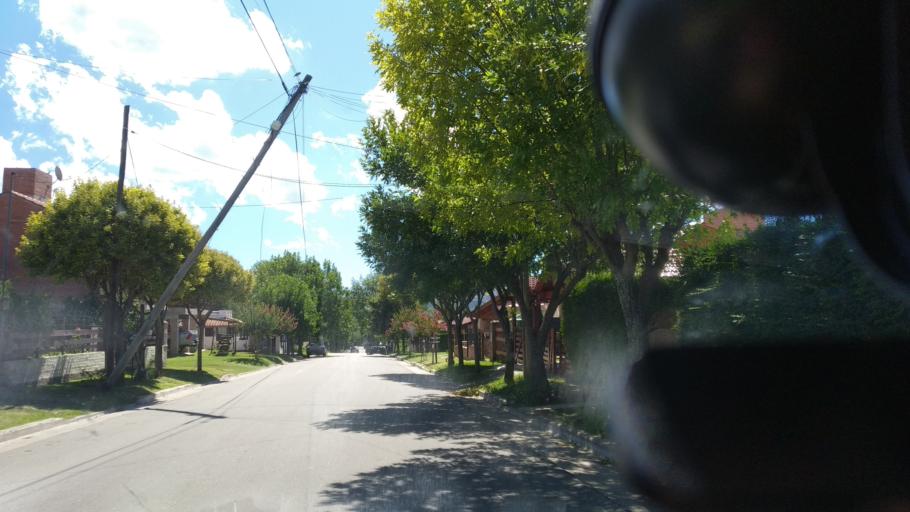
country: AR
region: Cordoba
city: Mina Clavero
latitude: -31.7241
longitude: -65.0097
